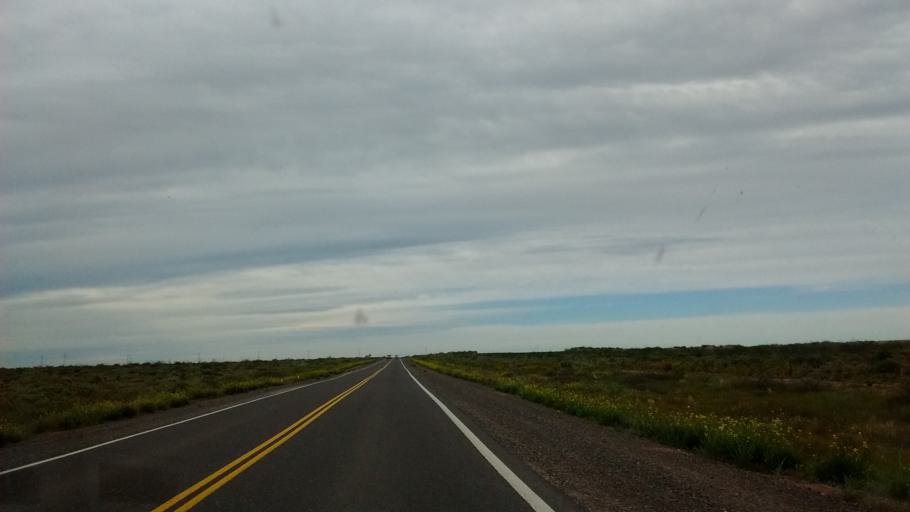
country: AR
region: Rio Negro
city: Catriel
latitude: -38.2157
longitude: -67.9781
